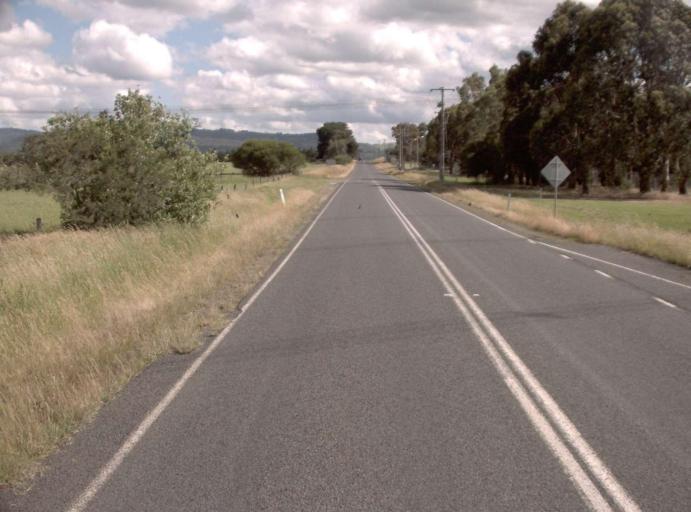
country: AU
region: Victoria
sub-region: Latrobe
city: Morwell
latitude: -38.2808
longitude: 146.4316
